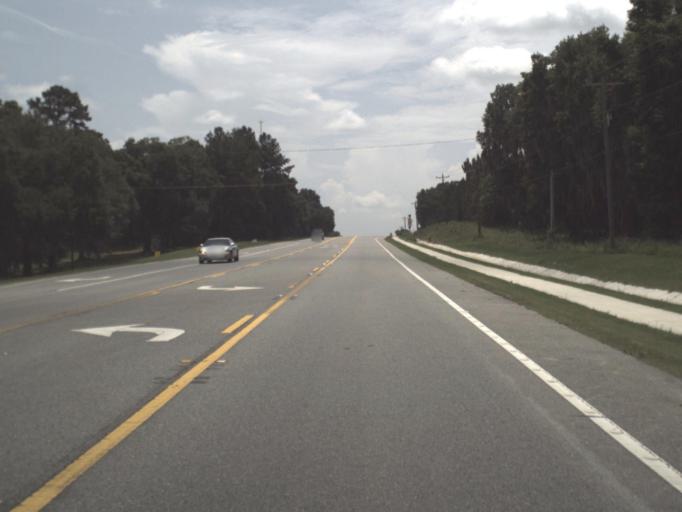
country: US
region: Florida
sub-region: Madison County
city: Madison
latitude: 30.4858
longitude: -83.4560
